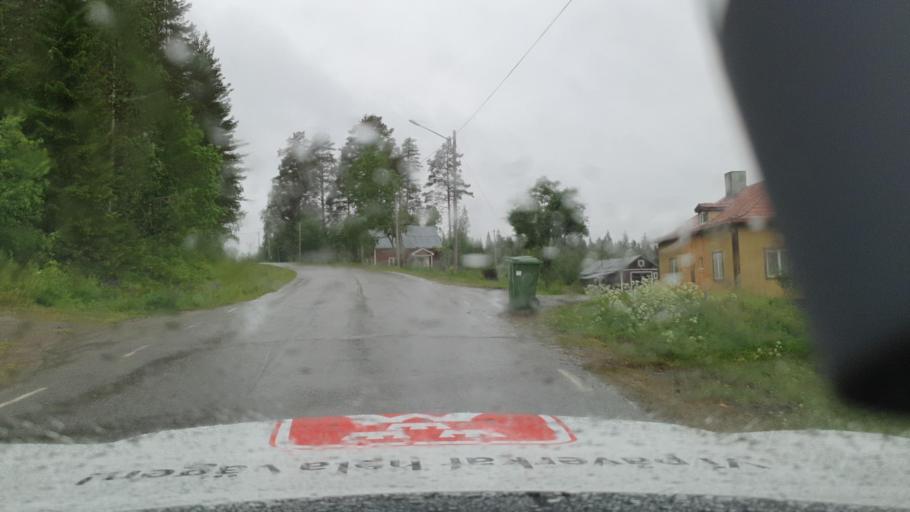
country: SE
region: Vaesterbotten
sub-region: Lycksele Kommun
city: Lycksele
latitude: 64.0731
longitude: 18.3837
